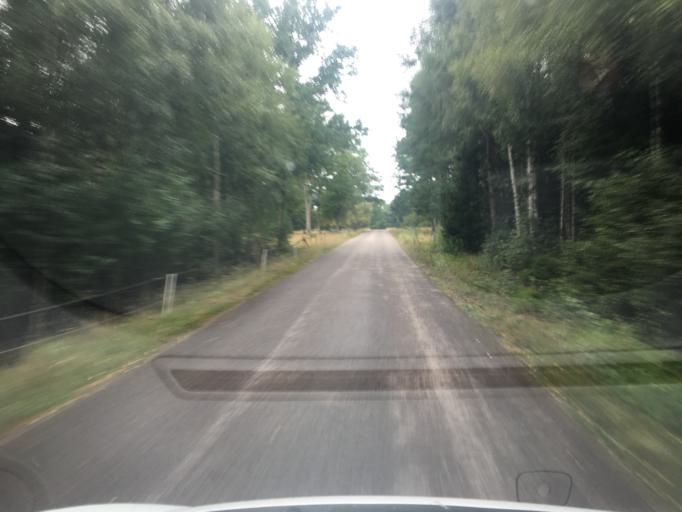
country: SE
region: Kronoberg
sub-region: Ljungby Kommun
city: Lagan
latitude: 56.9879
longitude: 14.0171
